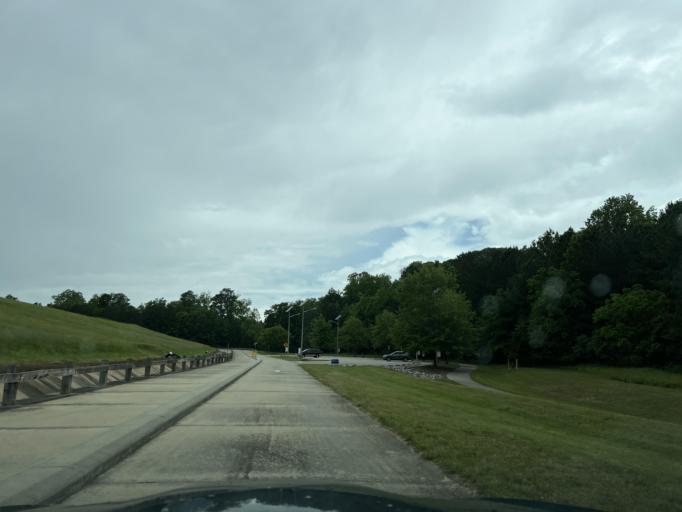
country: US
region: North Carolina
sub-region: Wake County
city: Wake Forest
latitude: 35.9098
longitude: -78.5786
